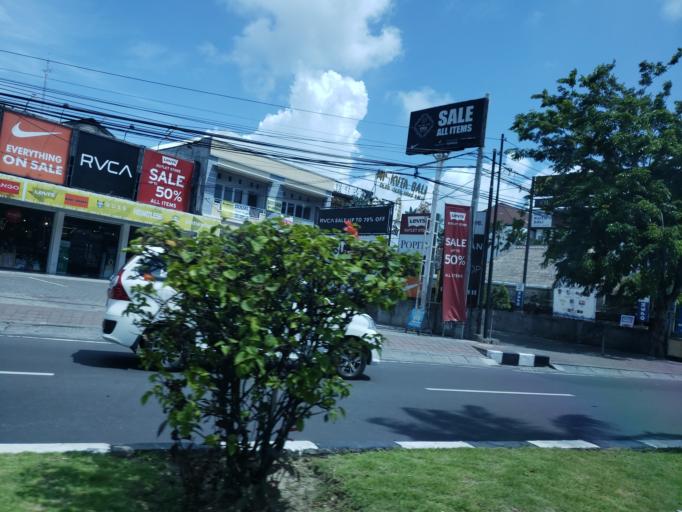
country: ID
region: Bali
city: Jabajero
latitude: -8.7264
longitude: 115.1804
